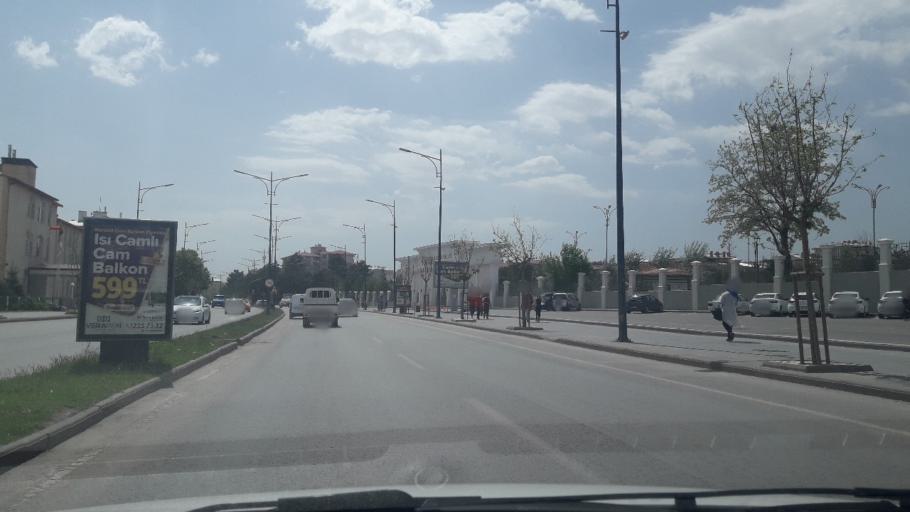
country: TR
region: Sivas
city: Sivas
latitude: 39.7399
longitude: 37.0044
